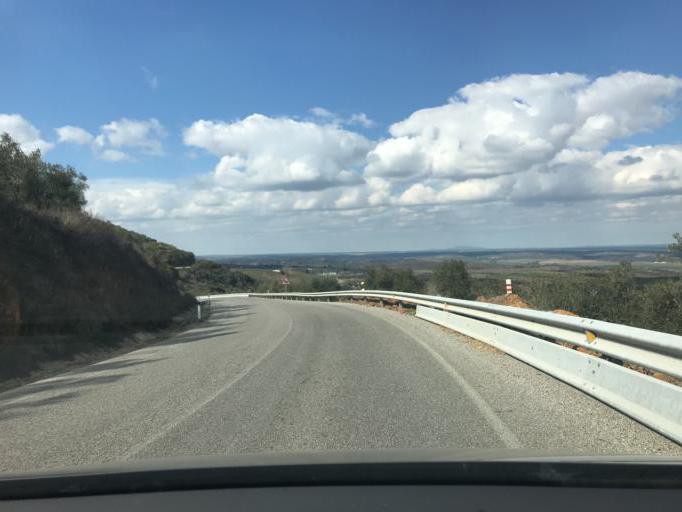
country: ES
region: Andalusia
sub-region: Provincia de Sevilla
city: Guadalcanal
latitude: 38.1060
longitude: -5.8163
